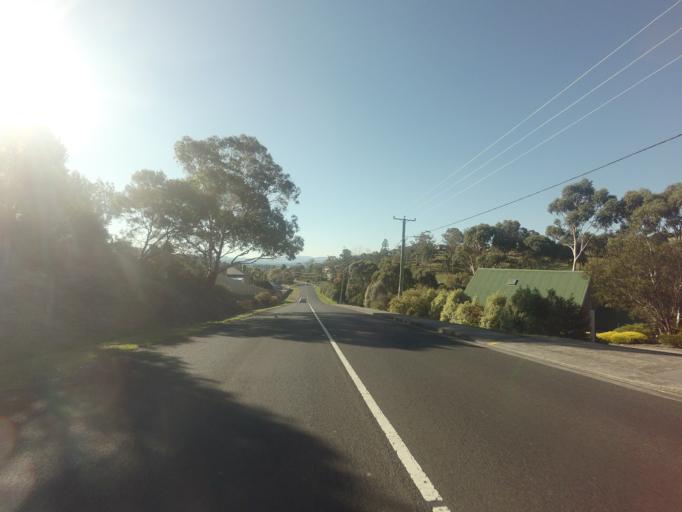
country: AU
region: Tasmania
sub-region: Glenorchy
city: West Moonah
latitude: -42.8548
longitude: 147.2682
